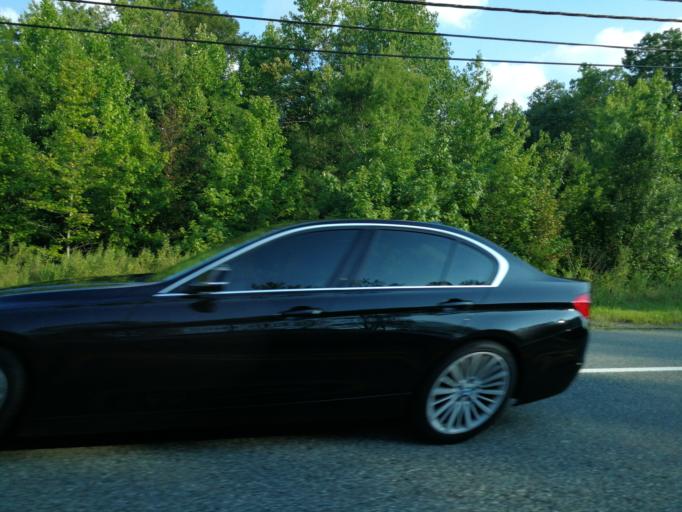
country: US
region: Maryland
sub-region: Harford County
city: Riverside
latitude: 39.4852
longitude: -76.2409
